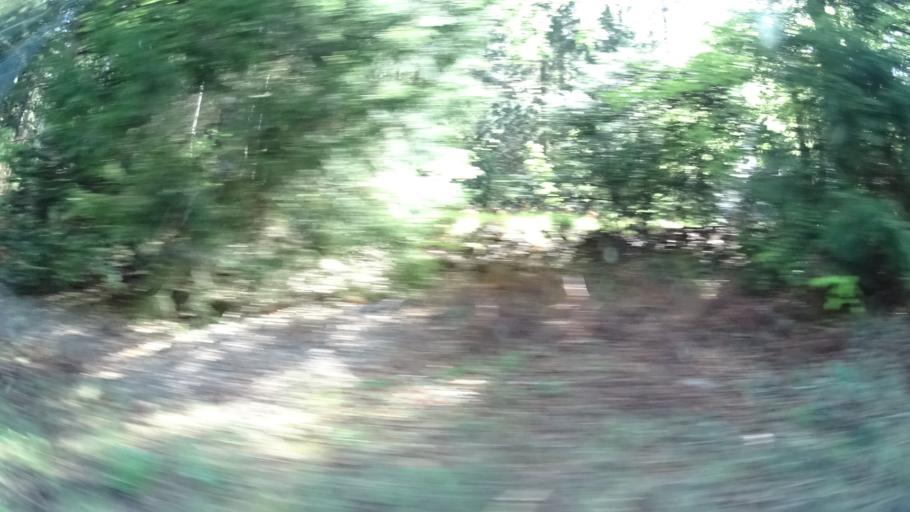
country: DE
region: Baden-Wuerttemberg
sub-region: Karlsruhe Region
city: Bad Wildbad
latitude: 48.7162
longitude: 8.5616
